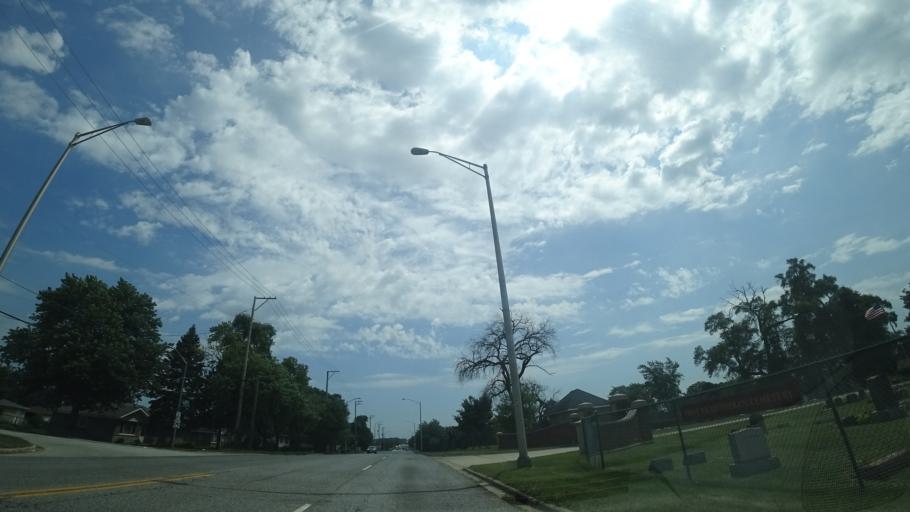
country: US
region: Illinois
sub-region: Cook County
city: Alsip
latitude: 41.6619
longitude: -87.7262
